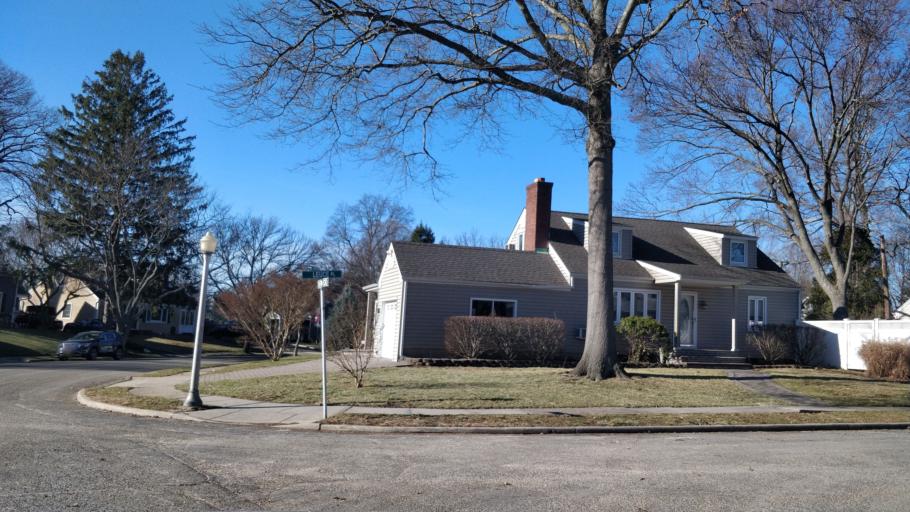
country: US
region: New York
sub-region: Nassau County
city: Glen Cove
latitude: 40.8764
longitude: -73.6260
